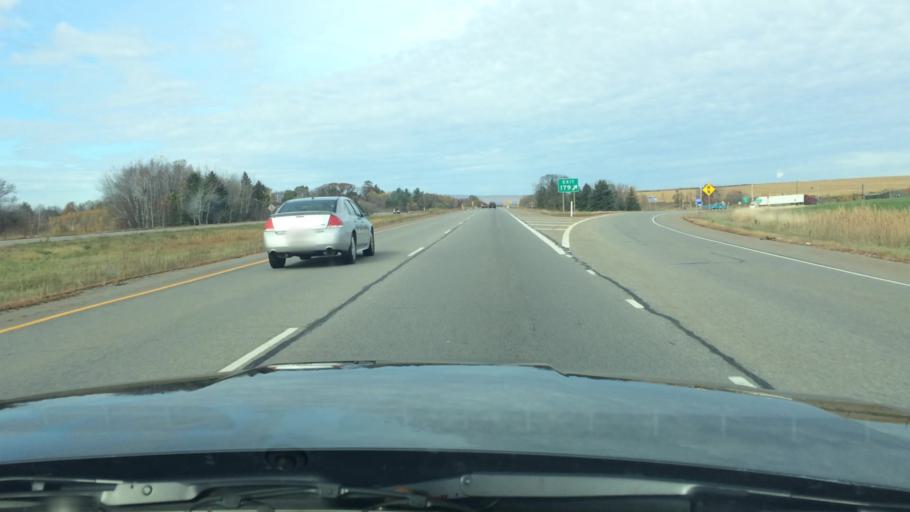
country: US
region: Wisconsin
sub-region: Marathon County
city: Mosinee
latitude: 44.7831
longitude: -89.6802
